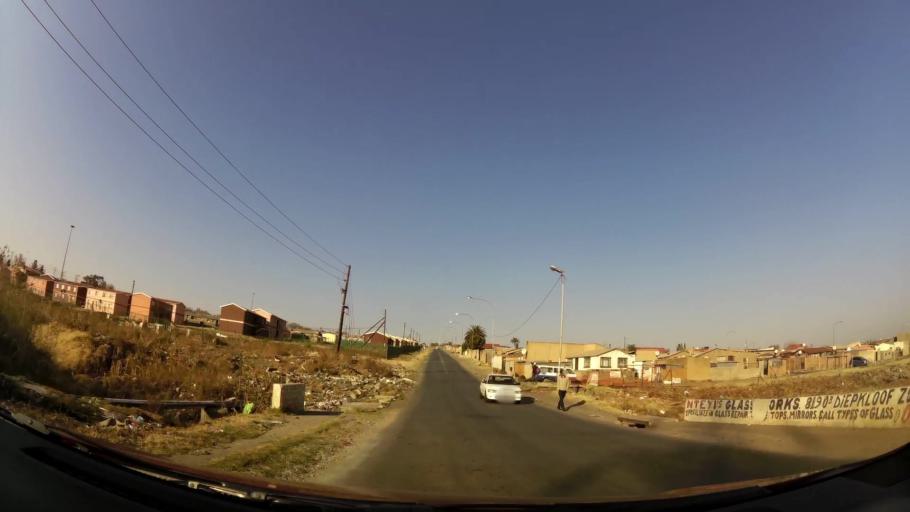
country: ZA
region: Gauteng
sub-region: City of Johannesburg Metropolitan Municipality
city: Soweto
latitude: -26.2565
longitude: 27.9521
